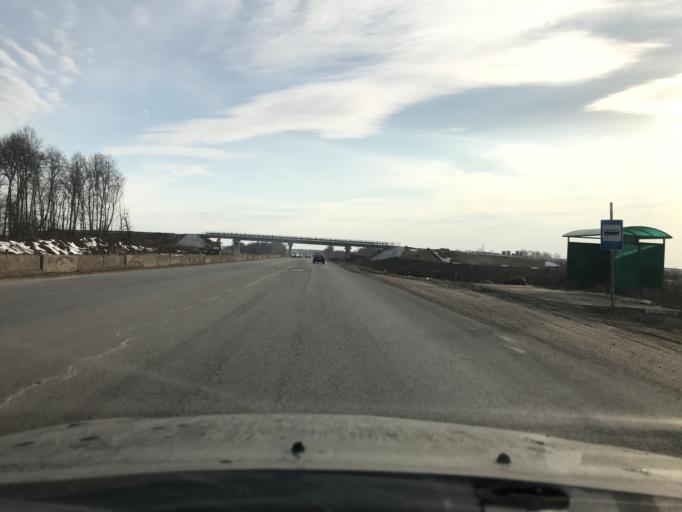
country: RU
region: Kaluga
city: Kaluga
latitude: 54.4383
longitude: 36.2219
